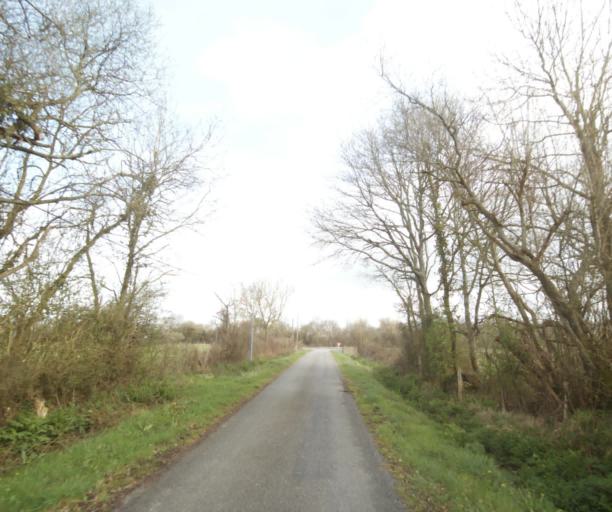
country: FR
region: Pays de la Loire
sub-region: Departement de la Loire-Atlantique
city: Bouvron
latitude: 47.4173
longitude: -1.8751
